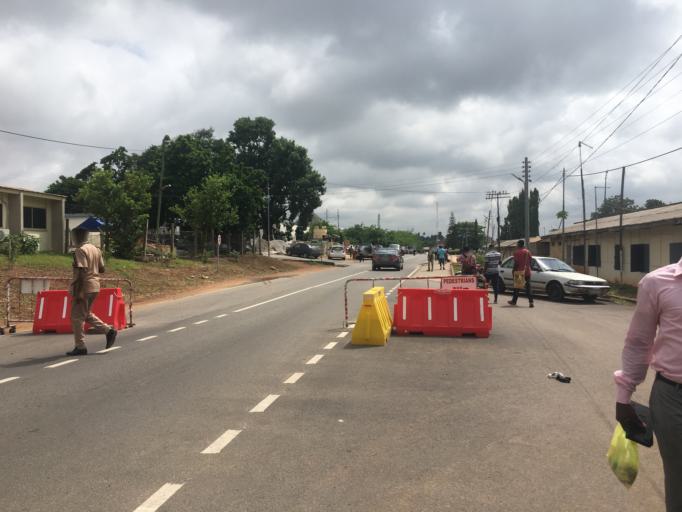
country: GH
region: Ashanti
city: Kumasi
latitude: 6.6852
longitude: -1.5751
